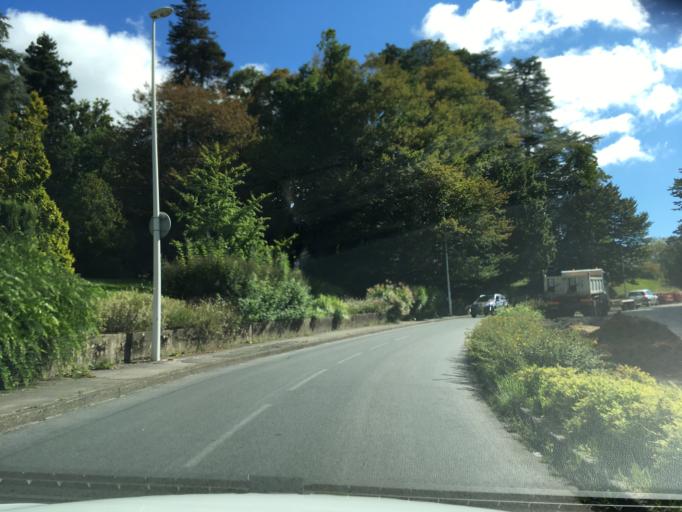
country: FR
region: Aquitaine
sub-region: Departement des Pyrenees-Atlantiques
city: Bayonne
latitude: 43.4999
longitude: -1.4626
